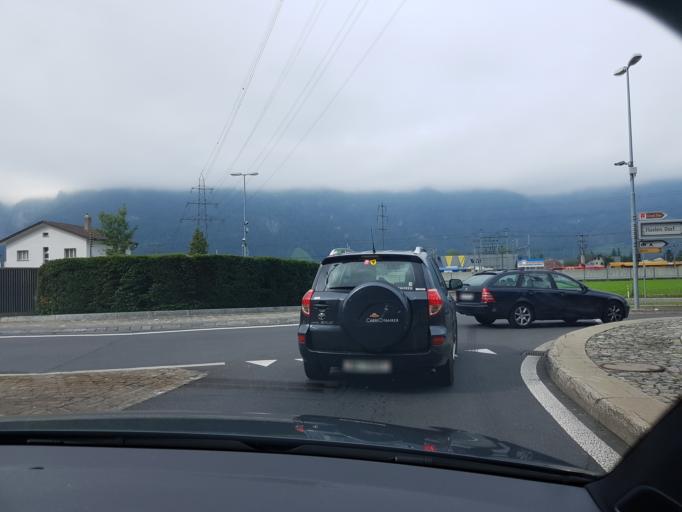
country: CH
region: Uri
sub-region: Uri
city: Flueelen
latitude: 46.8947
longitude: 8.6252
